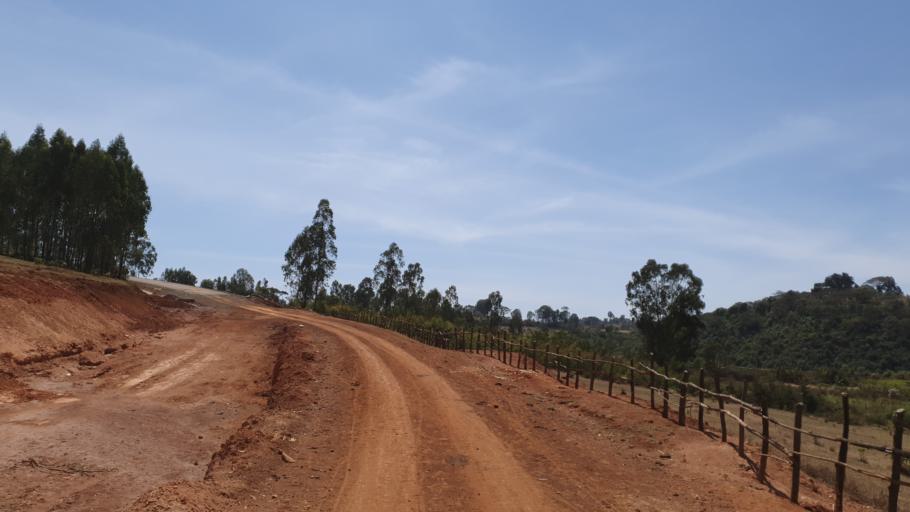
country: ET
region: Oromiya
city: Shambu
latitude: 9.8871
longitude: 36.6501
